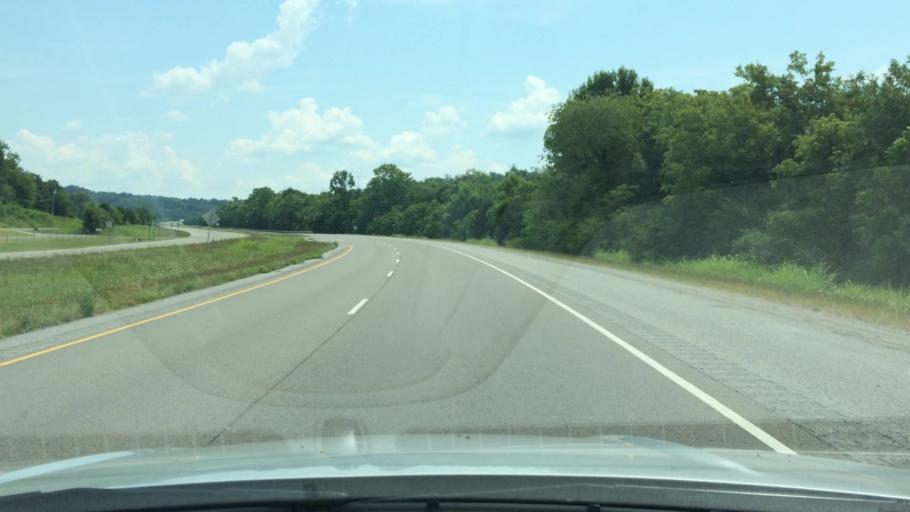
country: US
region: Tennessee
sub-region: Giles County
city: Pulaski
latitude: 35.1700
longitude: -87.0139
